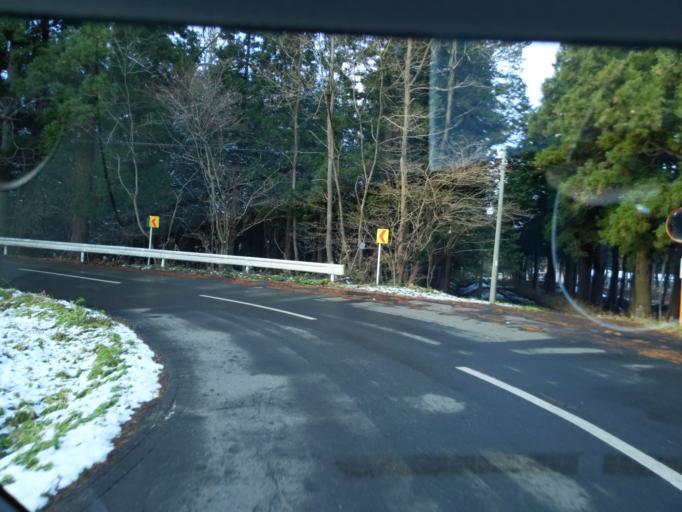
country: JP
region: Iwate
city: Kitakami
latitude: 39.2358
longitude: 141.0401
